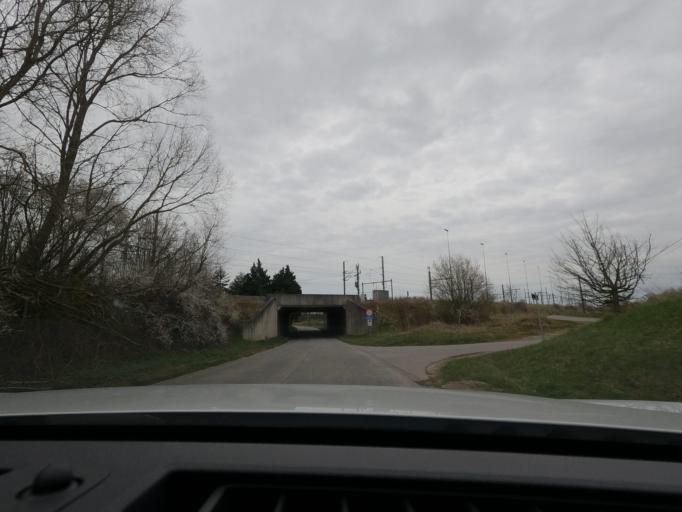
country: BE
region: Wallonia
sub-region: Province du Hainaut
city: Brugelette
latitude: 50.6323
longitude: 3.8624
